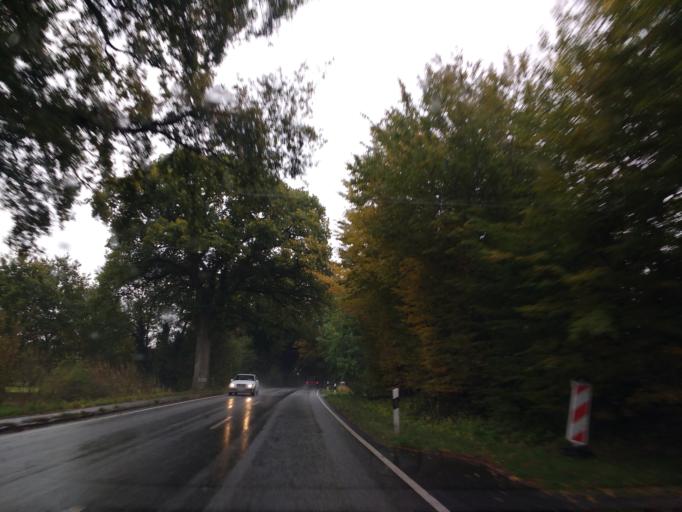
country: DE
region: Schleswig-Holstein
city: Susel
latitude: 54.1048
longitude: 10.6664
